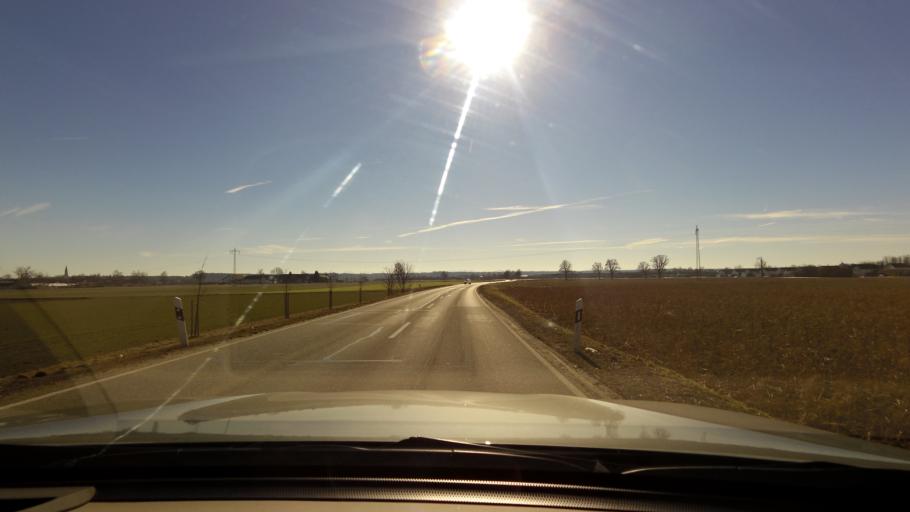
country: DE
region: Bavaria
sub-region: Upper Bavaria
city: Neufahrn
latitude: 48.2612
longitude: 12.4330
